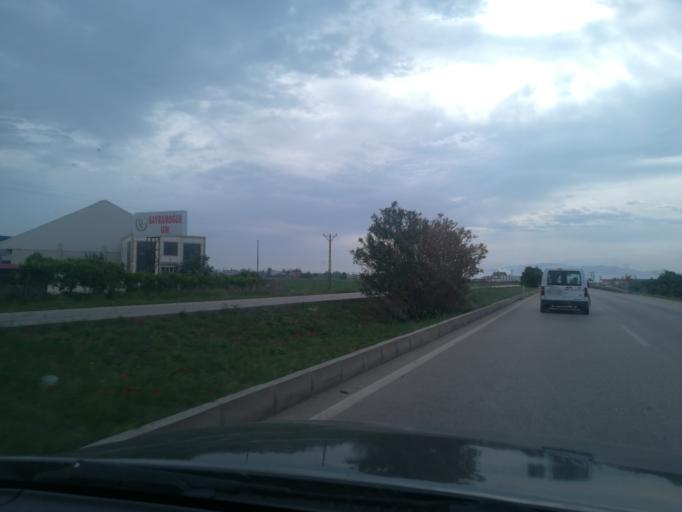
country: TR
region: Adana
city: Yakapinar
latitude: 36.9683
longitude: 35.5525
